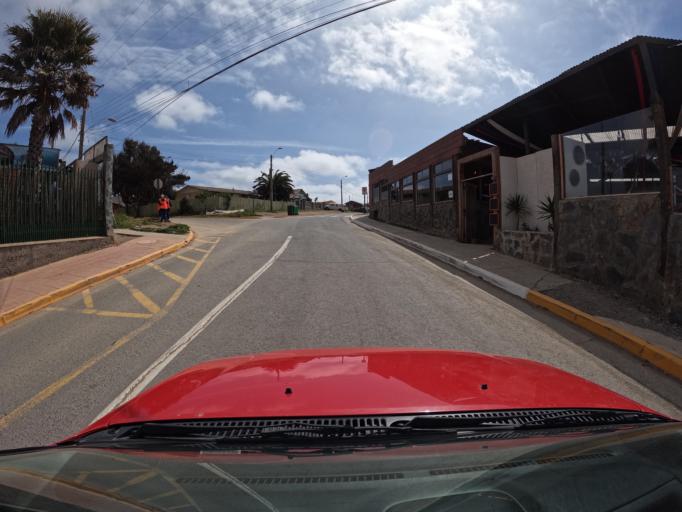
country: CL
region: O'Higgins
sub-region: Provincia de Colchagua
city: Santa Cruz
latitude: -34.3835
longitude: -72.0144
